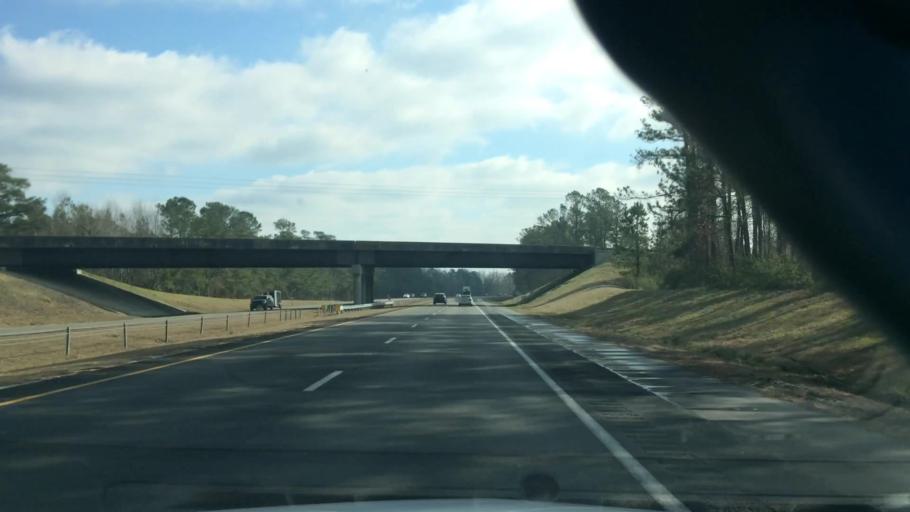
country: US
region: North Carolina
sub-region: Pender County
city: Burgaw
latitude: 34.6125
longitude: -77.9213
